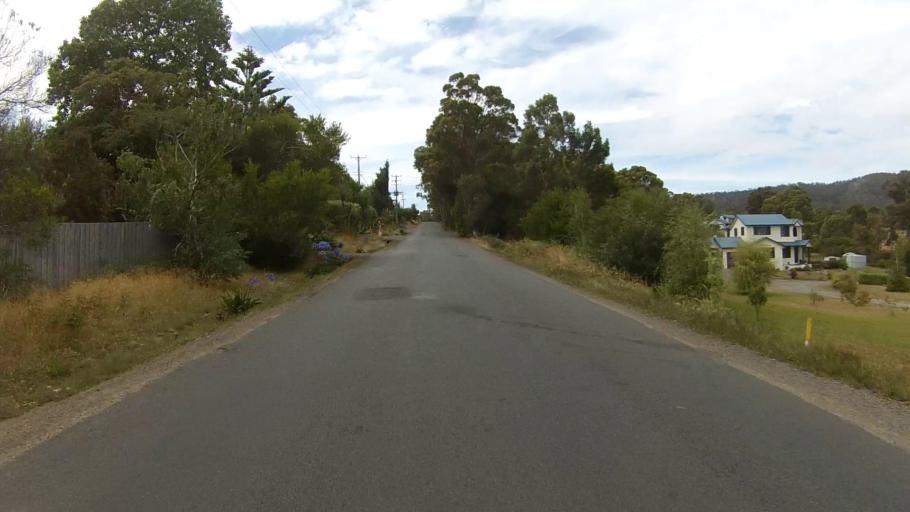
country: AU
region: Tasmania
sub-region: Kingborough
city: Blackmans Bay
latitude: -43.0252
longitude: 147.2960
